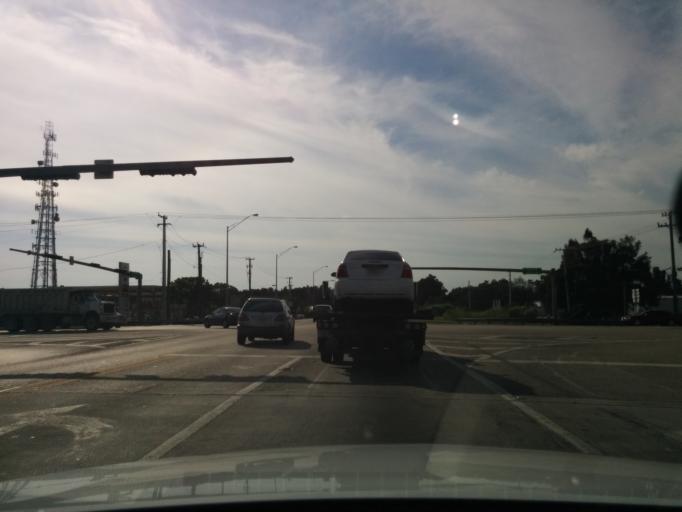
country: US
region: Florida
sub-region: Miami-Dade County
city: Kendall West
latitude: 25.7614
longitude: -80.4813
